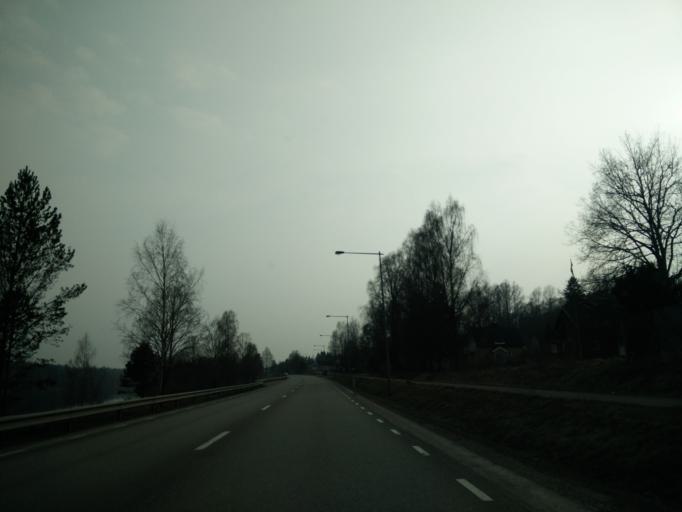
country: SE
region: Vaermland
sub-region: Forshaga Kommun
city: Forshaga
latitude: 59.5181
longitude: 13.4452
